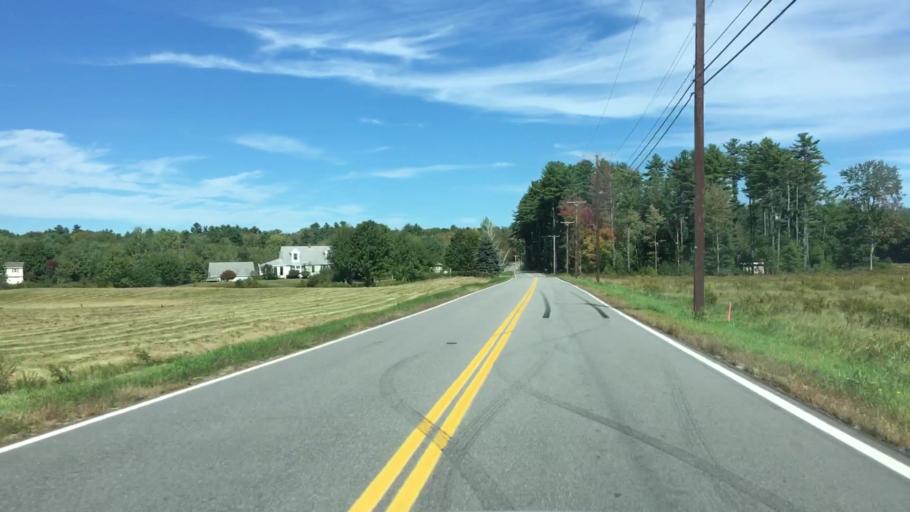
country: US
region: Maine
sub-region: York County
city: Saco
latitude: 43.5642
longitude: -70.4864
